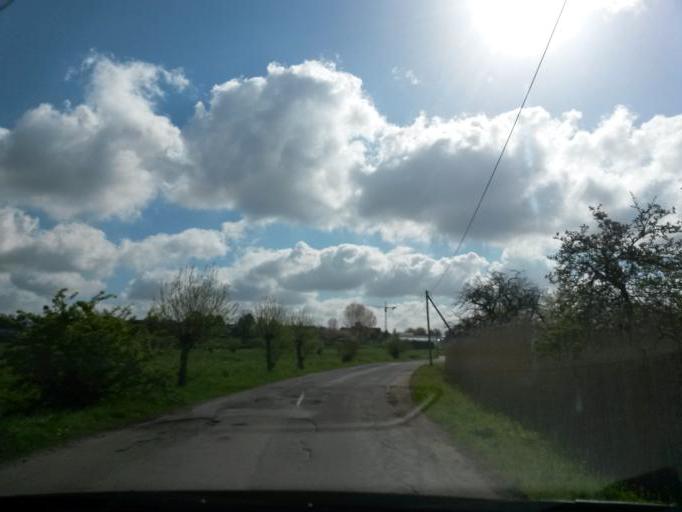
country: DE
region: Schleswig-Holstein
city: Wedel
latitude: 53.5868
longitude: 9.6822
